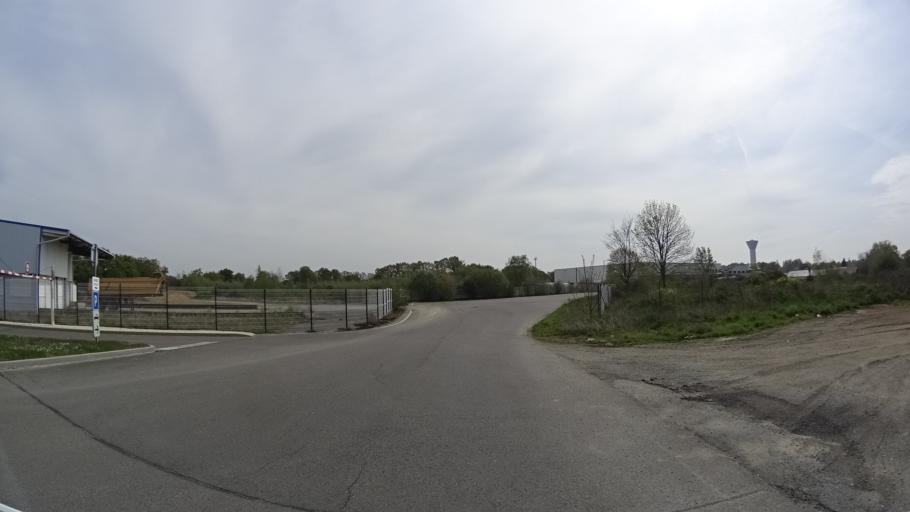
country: FR
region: Brittany
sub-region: Departement d'Ille-et-Vilaine
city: Bruz
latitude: 48.0359
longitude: -1.7340
